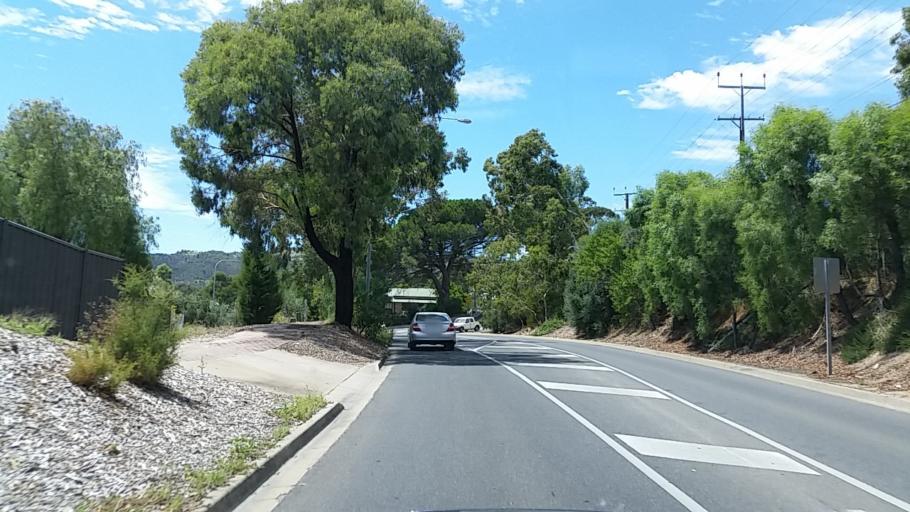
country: AU
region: South Australia
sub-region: Campbelltown
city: Athelstone
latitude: -34.8685
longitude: 138.7066
